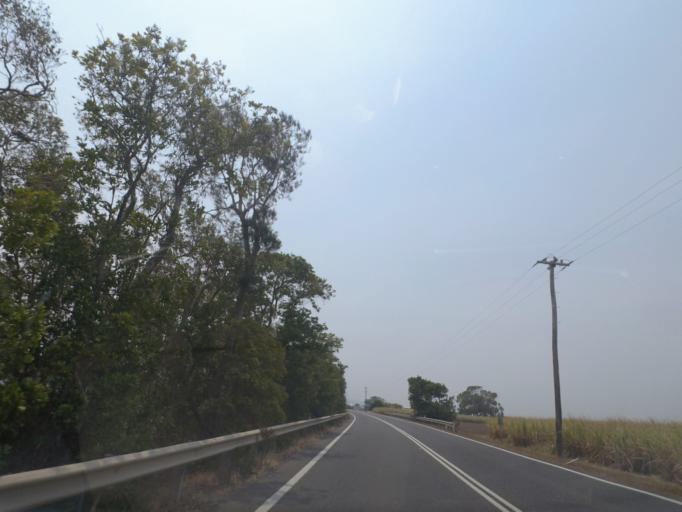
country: AU
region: New South Wales
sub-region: Richmond Valley
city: Evans Head
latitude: -28.9822
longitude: 153.4622
